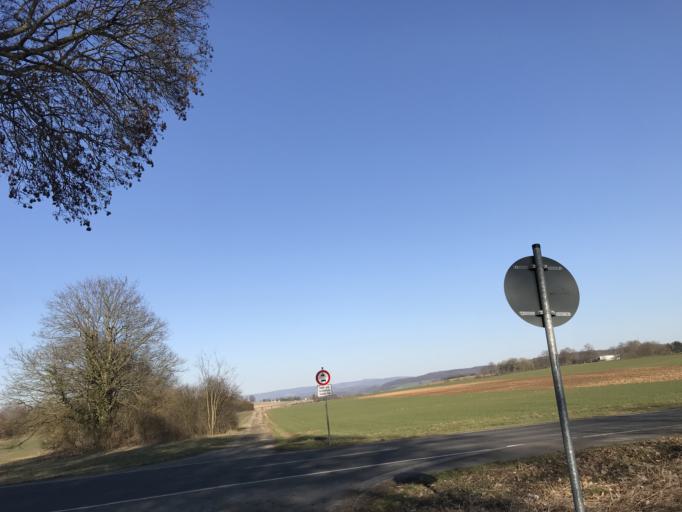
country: DE
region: Hesse
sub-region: Regierungsbezirk Darmstadt
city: Nidda
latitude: 50.4257
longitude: 8.9991
